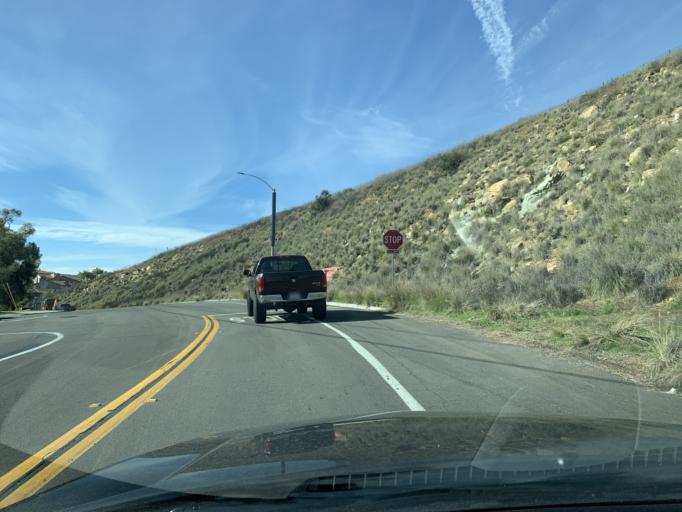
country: US
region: California
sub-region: San Diego County
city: Lemon Grove
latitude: 32.7480
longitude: -117.0309
